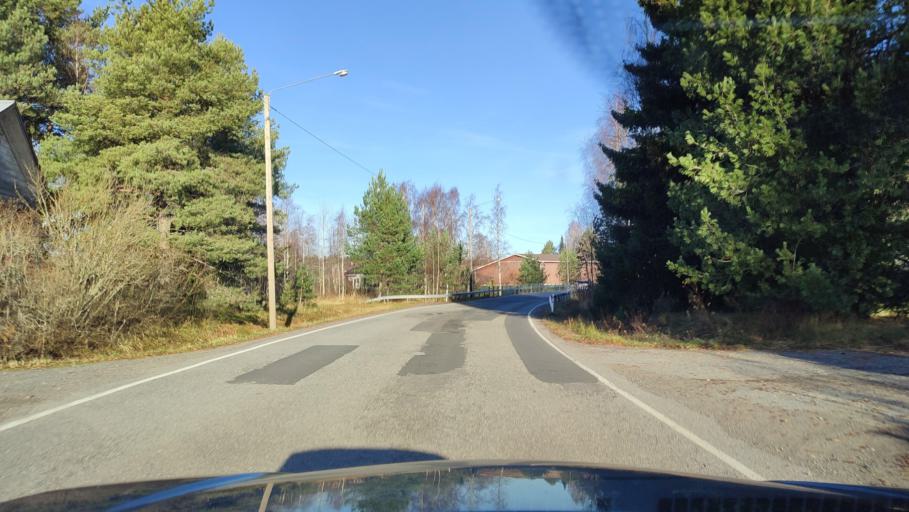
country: FI
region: Southern Ostrobothnia
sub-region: Suupohja
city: Karijoki
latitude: 62.2307
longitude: 21.6540
